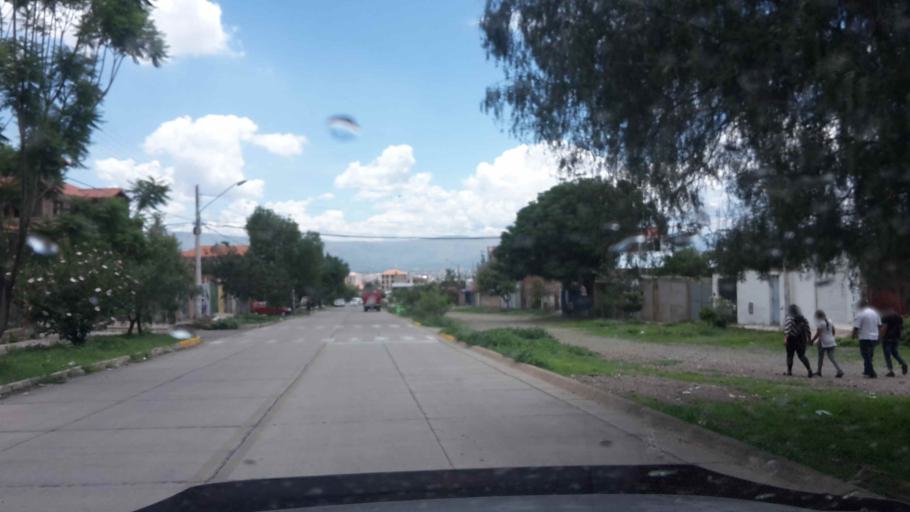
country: BO
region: Cochabamba
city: Cochabamba
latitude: -17.3495
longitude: -66.1816
